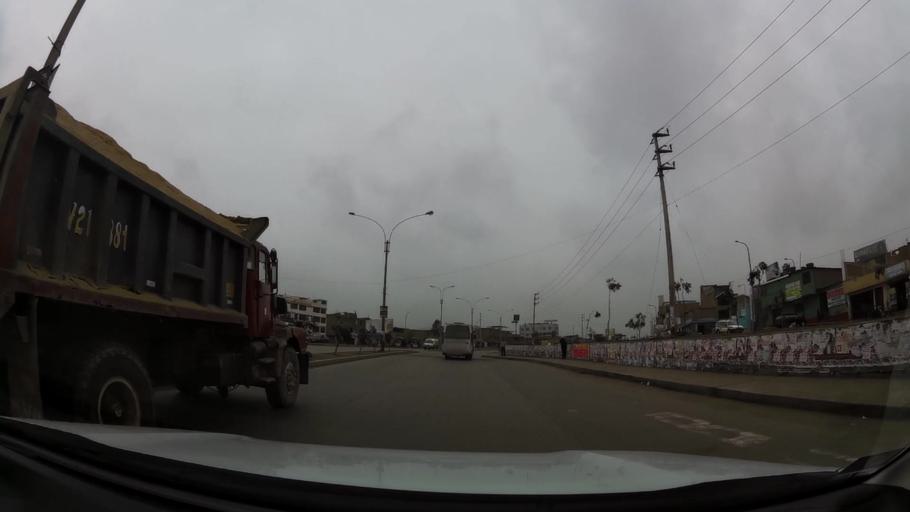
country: PE
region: Lima
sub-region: Lima
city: Punta Hermosa
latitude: -12.2391
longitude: -76.9125
